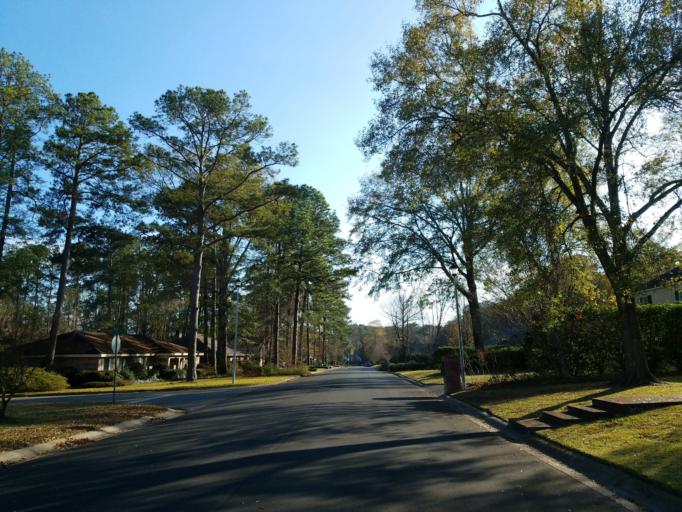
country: US
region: Mississippi
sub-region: Lamar County
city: West Hattiesburg
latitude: 31.3082
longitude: -89.3432
